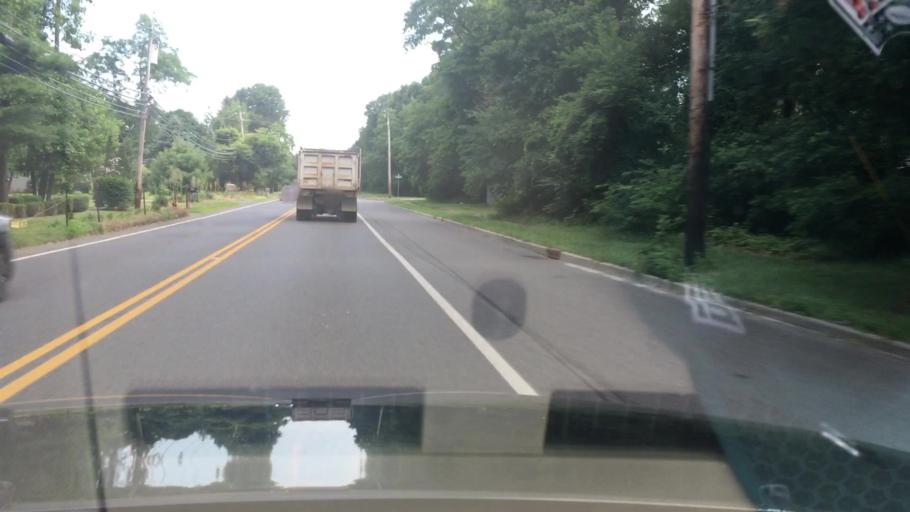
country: US
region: New Jersey
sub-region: Ocean County
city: Vista Center
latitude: 40.1462
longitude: -74.3975
